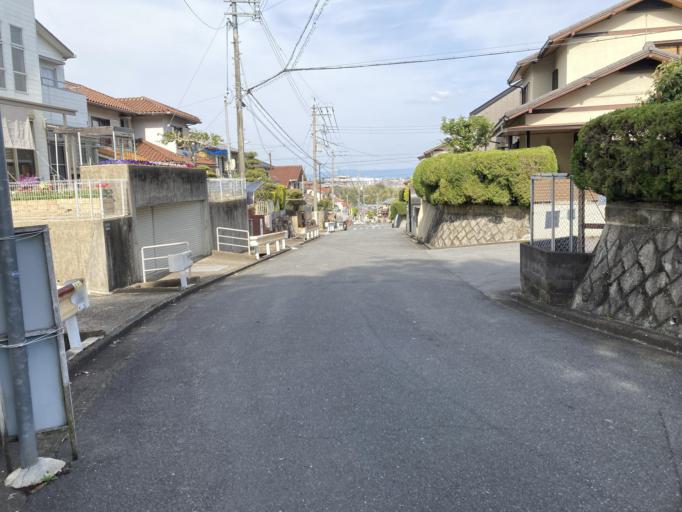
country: JP
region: Nara
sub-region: Ikoma-shi
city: Ikoma
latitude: 34.6832
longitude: 135.7257
